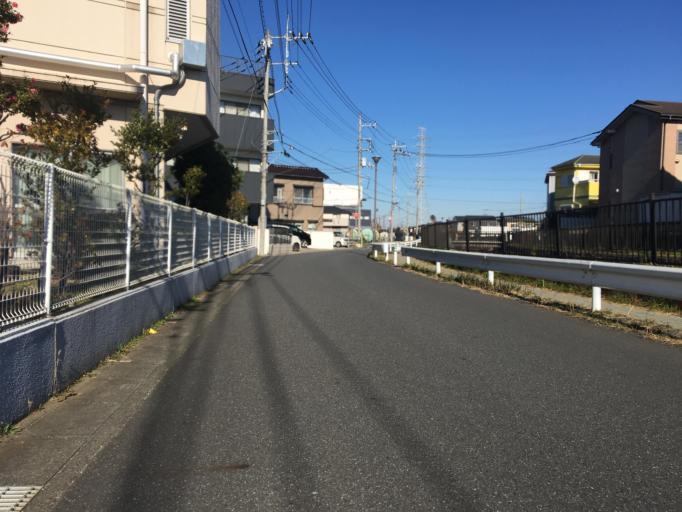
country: JP
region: Saitama
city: Yashio-shi
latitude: 35.8352
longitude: 139.8317
